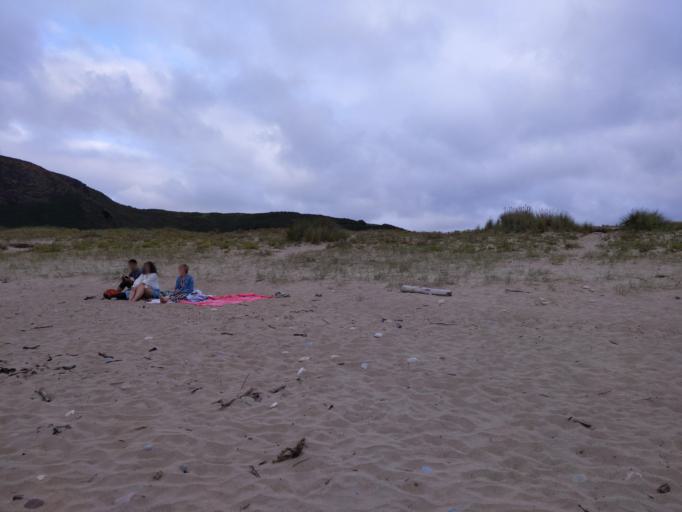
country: ES
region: Asturias
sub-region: Province of Asturias
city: Aviles
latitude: 43.6038
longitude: -5.9192
